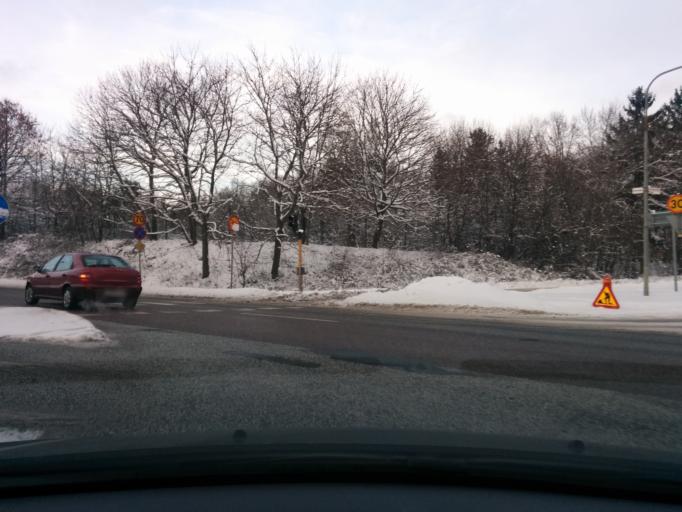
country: SE
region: Stockholm
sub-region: Stockholms Kommun
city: Arsta
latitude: 59.2739
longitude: 18.0449
